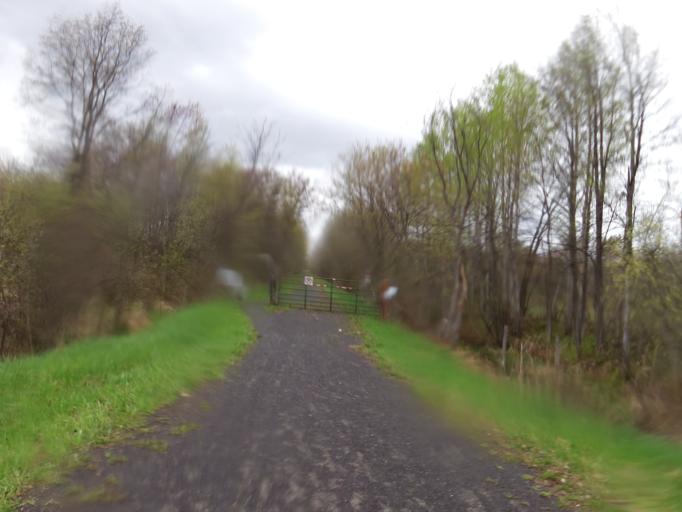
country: CA
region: Ontario
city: Bourget
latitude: 45.4376
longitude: -75.2166
